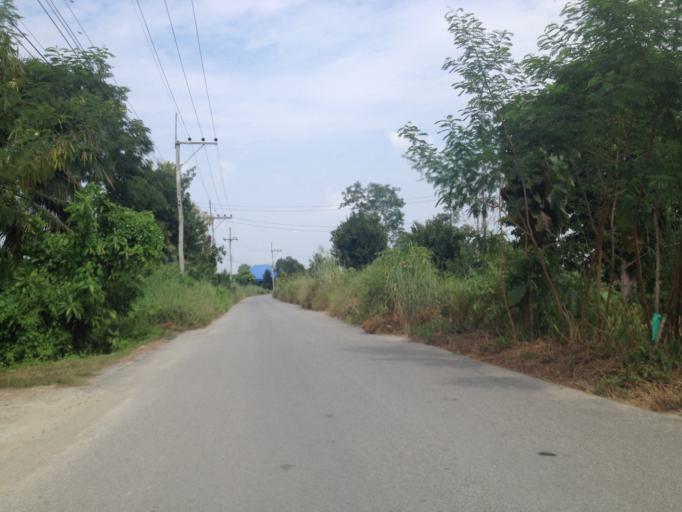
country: TH
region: Chiang Mai
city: San Pa Tong
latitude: 18.6434
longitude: 98.8515
